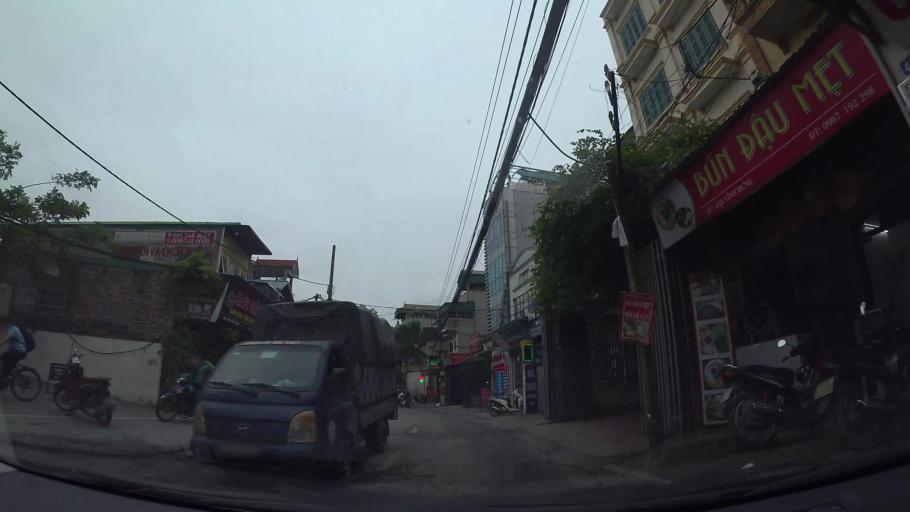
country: VN
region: Ha Noi
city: Hai BaTrung
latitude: 20.9987
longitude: 105.8796
